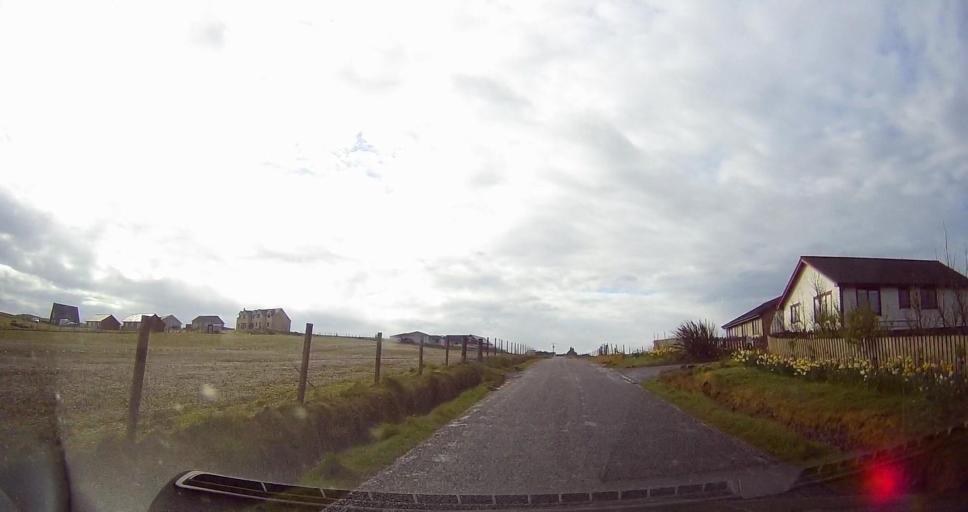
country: GB
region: Scotland
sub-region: Shetland Islands
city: Sandwick
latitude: 60.0594
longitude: -1.2148
